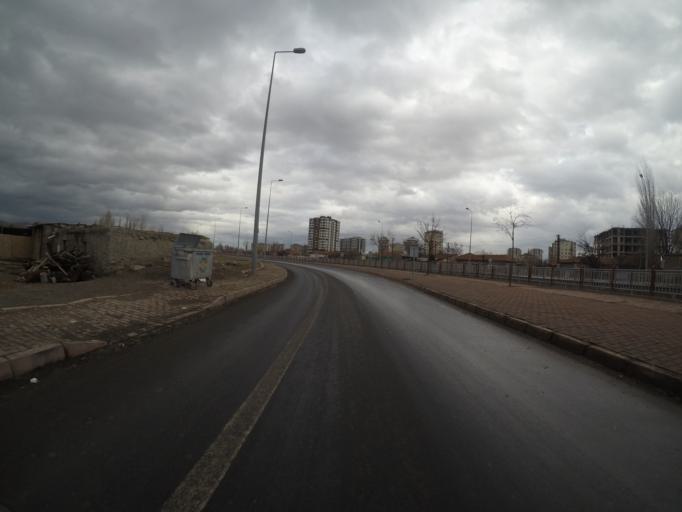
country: TR
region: Kayseri
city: Kayseri
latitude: 38.7507
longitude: 35.4752
